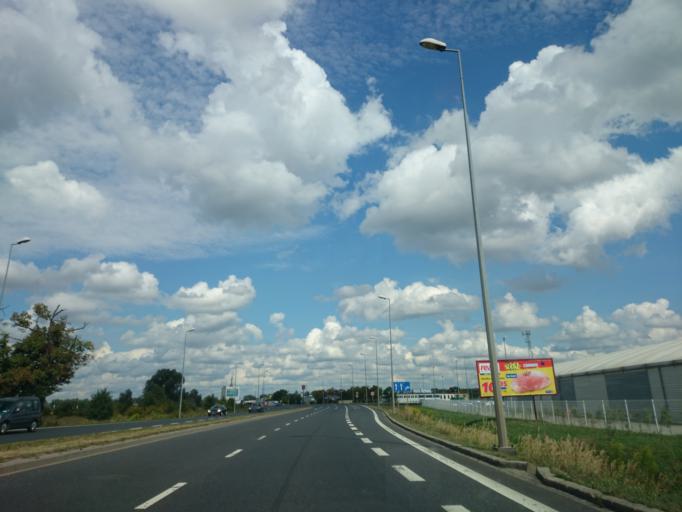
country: PL
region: Lower Silesian Voivodeship
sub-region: Legnica
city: Legnica
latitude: 51.1661
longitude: 16.1728
